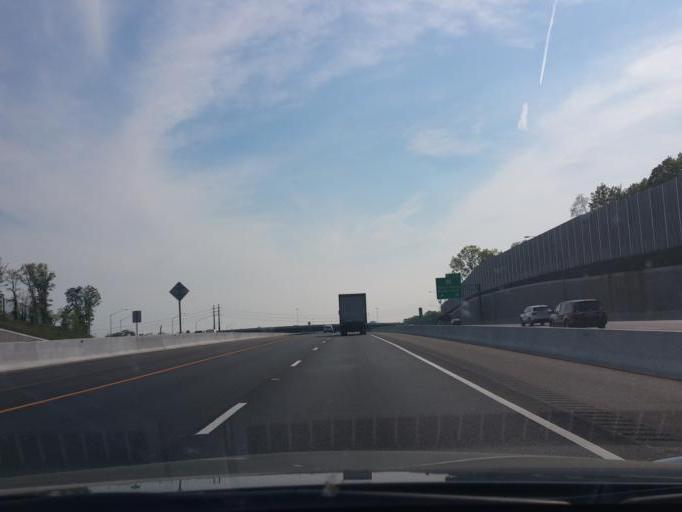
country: US
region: Maryland
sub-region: Baltimore County
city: White Marsh
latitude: 39.3845
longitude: -76.4435
